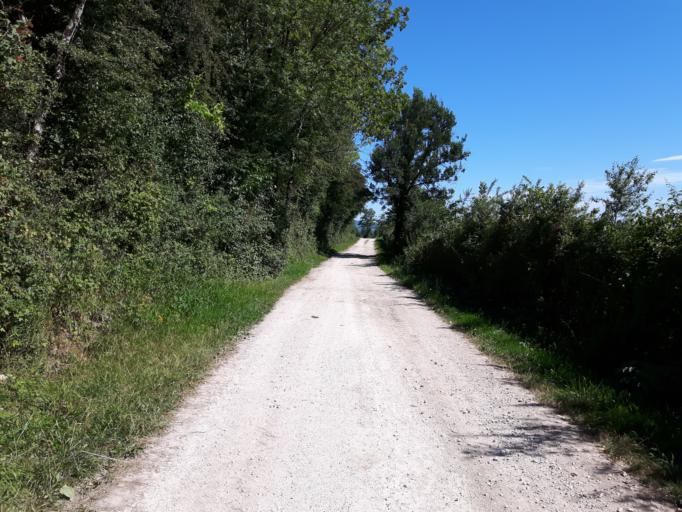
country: FR
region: Franche-Comte
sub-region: Departement du Jura
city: Mouchard
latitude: 47.0180
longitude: 5.8505
